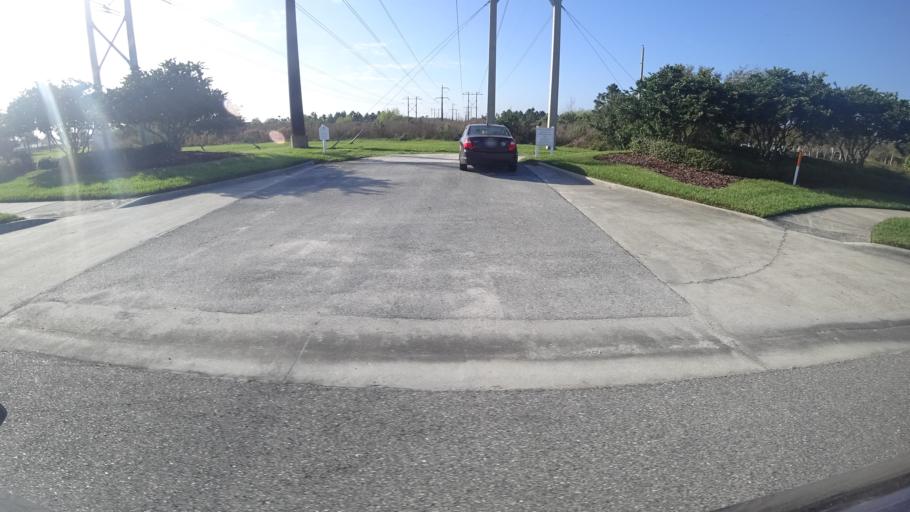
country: US
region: Florida
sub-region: Manatee County
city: Ellenton
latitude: 27.5664
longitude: -82.4593
